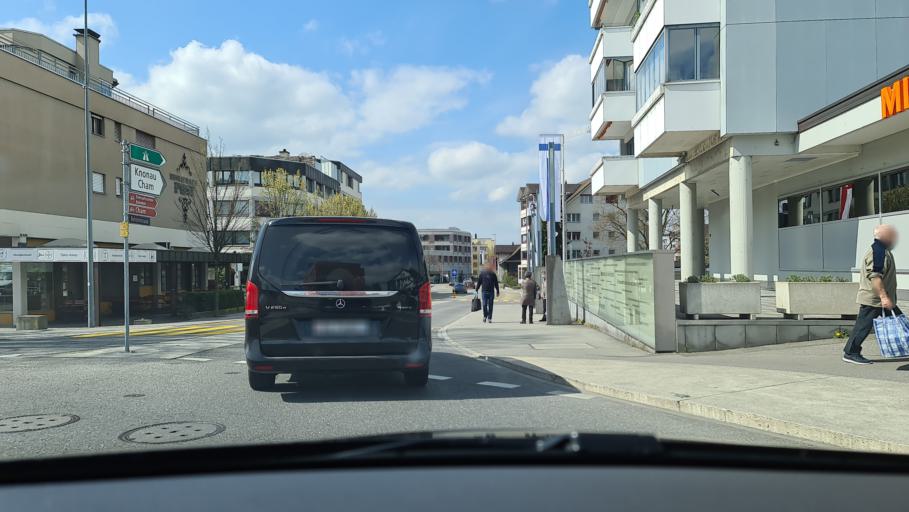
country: CH
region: Zug
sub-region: Zug
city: Steinhausen
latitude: 47.1970
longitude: 8.4852
